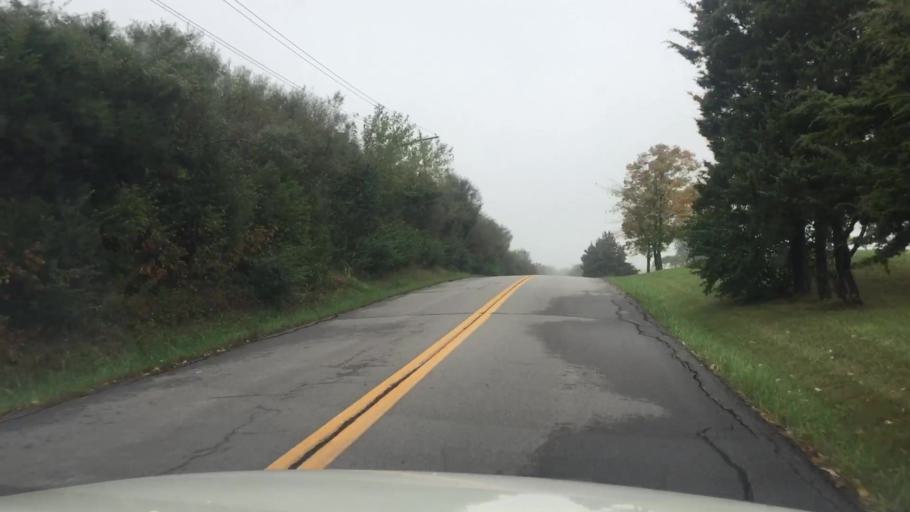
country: US
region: Missouri
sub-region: Boone County
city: Ashland
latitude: 38.8535
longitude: -92.3059
